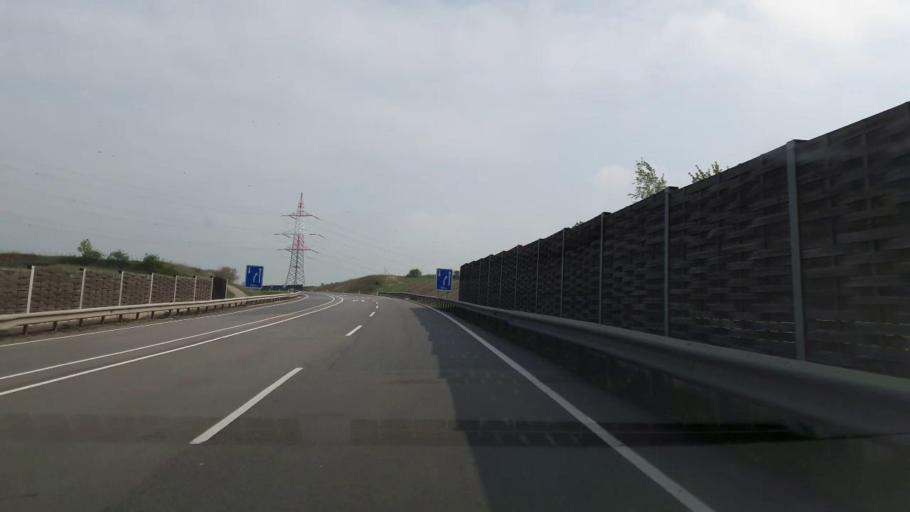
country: AT
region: Lower Austria
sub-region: Politischer Bezirk Hollabrunn
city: Haugsdorf
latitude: 48.7338
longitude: 16.0574
